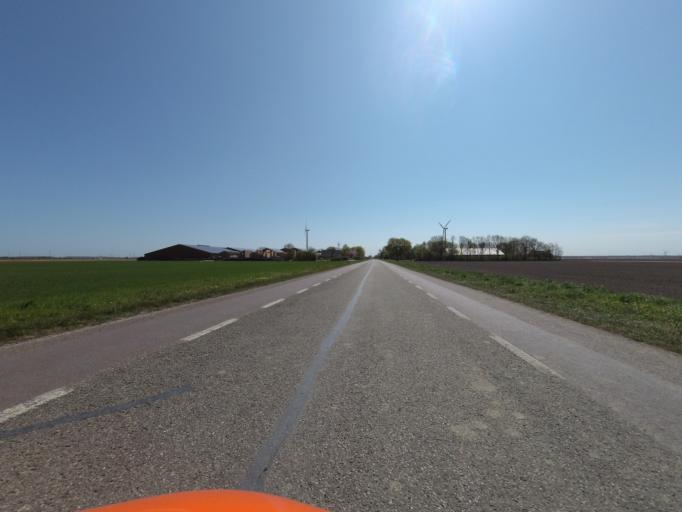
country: NL
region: Flevoland
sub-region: Gemeente Lelystad
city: Lelystad
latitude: 52.4095
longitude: 5.4163
